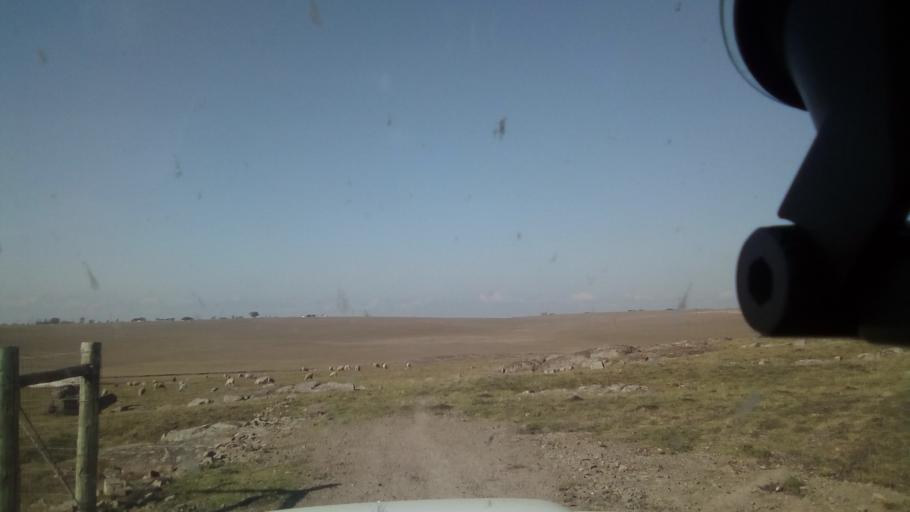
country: ZA
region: Eastern Cape
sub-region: Buffalo City Metropolitan Municipality
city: Bhisho
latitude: -32.9533
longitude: 27.3217
